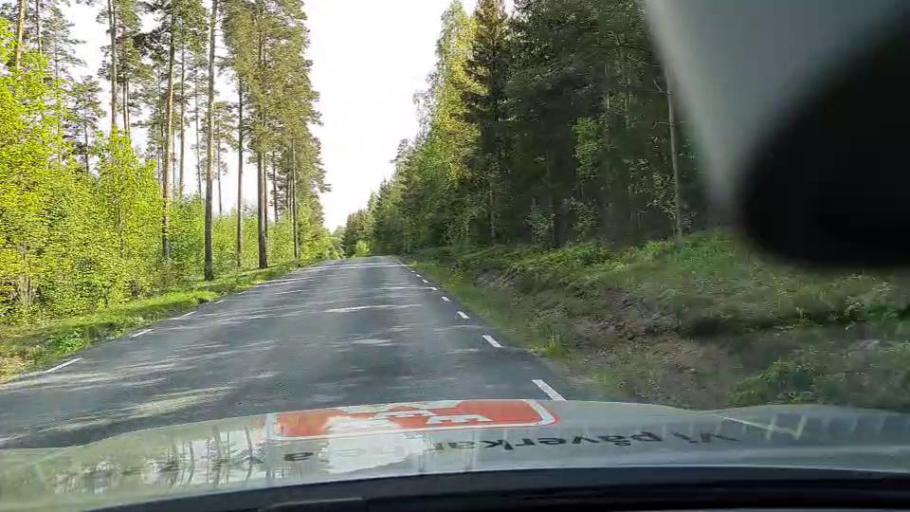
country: SE
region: Soedermanland
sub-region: Eskilstuna Kommun
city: Arla
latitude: 59.2577
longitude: 16.7118
